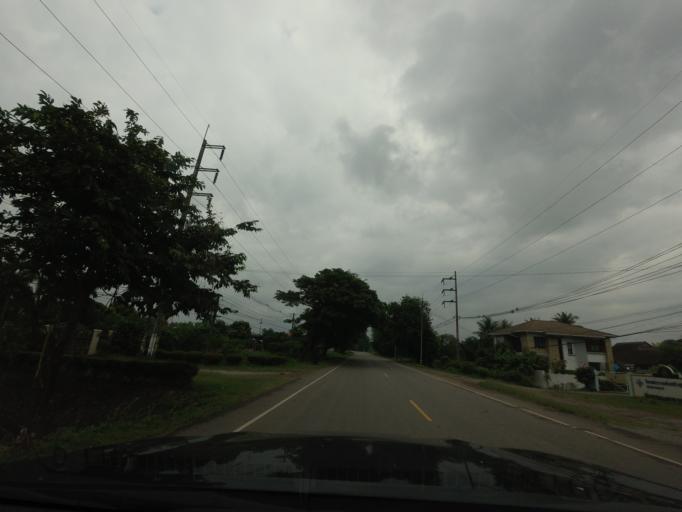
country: TH
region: Nong Khai
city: Si Chiang Mai
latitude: 17.9044
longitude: 102.6065
